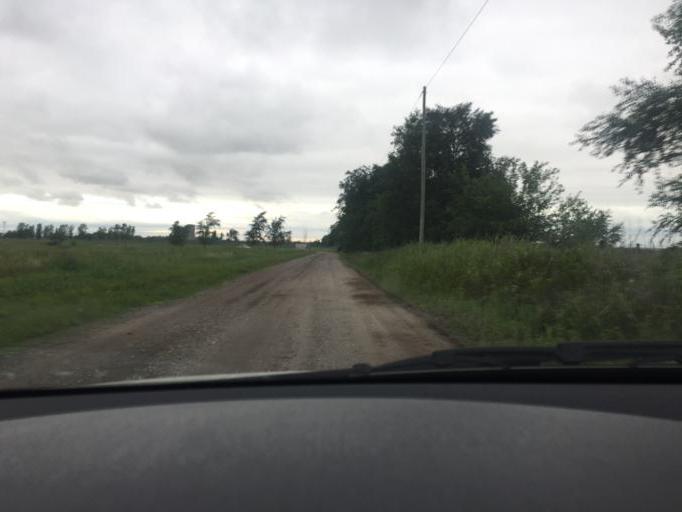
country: AR
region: Cordoba
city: Villa Allende
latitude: -31.3108
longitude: -64.2257
